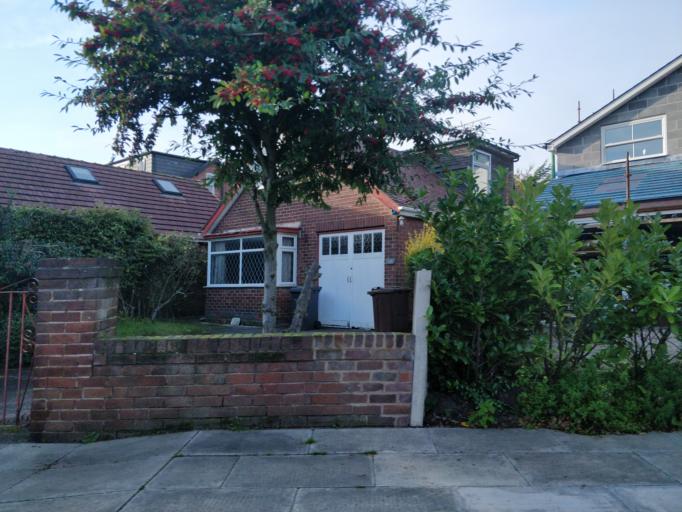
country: GB
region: England
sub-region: Lancashire
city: Banks
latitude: 53.6697
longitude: -2.9610
